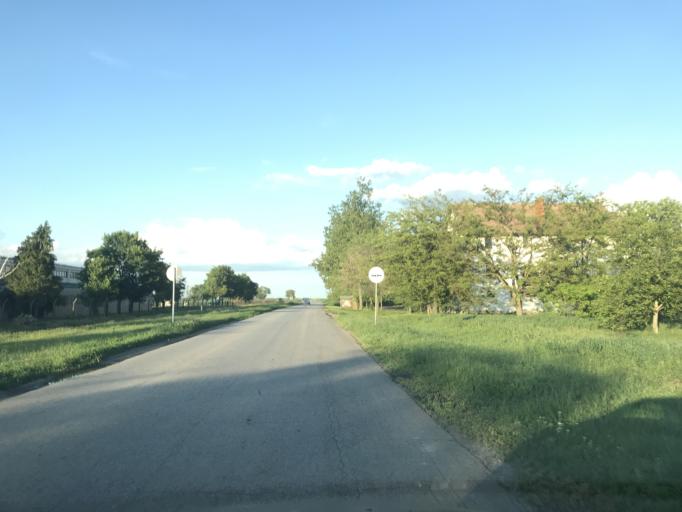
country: RS
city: Mihajlovo
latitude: 45.4475
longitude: 20.3927
